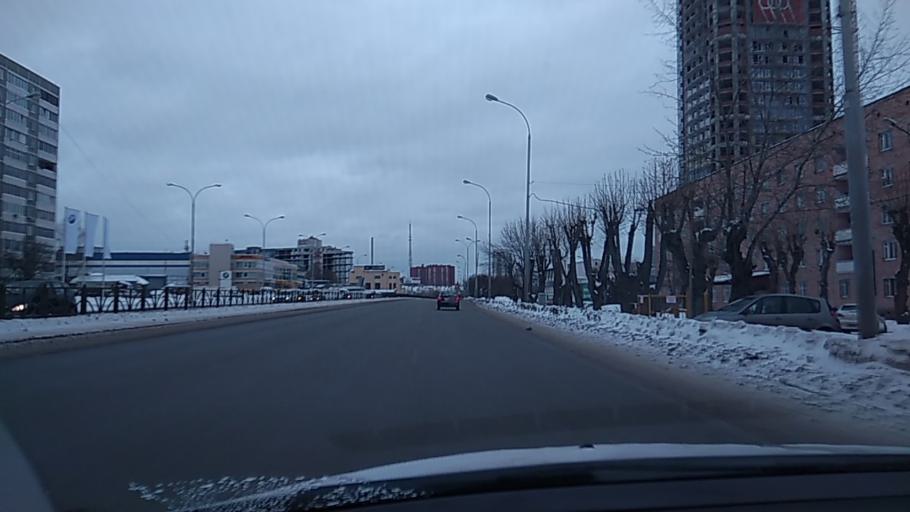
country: RU
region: Sverdlovsk
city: Yekaterinburg
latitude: 56.8116
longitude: 60.6296
